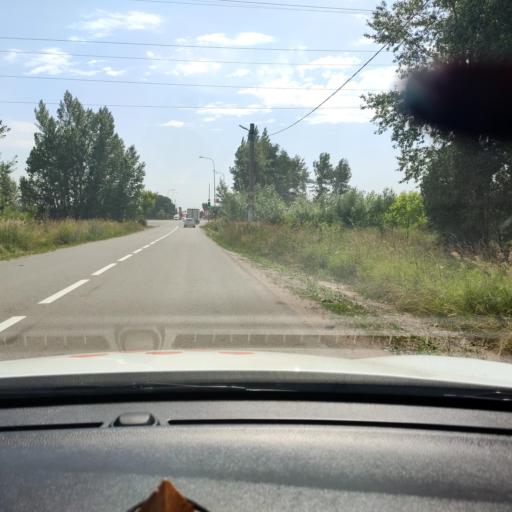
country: RU
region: Tatarstan
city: Osinovo
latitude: 55.9045
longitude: 48.9627
